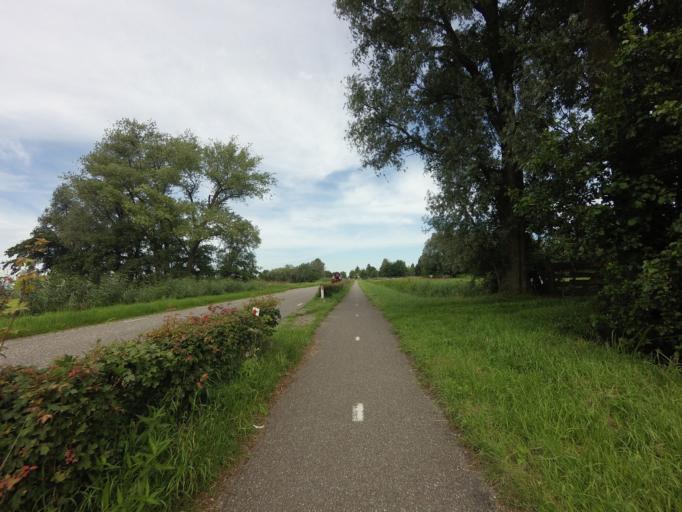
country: NL
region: Utrecht
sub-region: Stichtse Vecht
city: Breukelen
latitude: 52.1497
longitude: 4.9704
